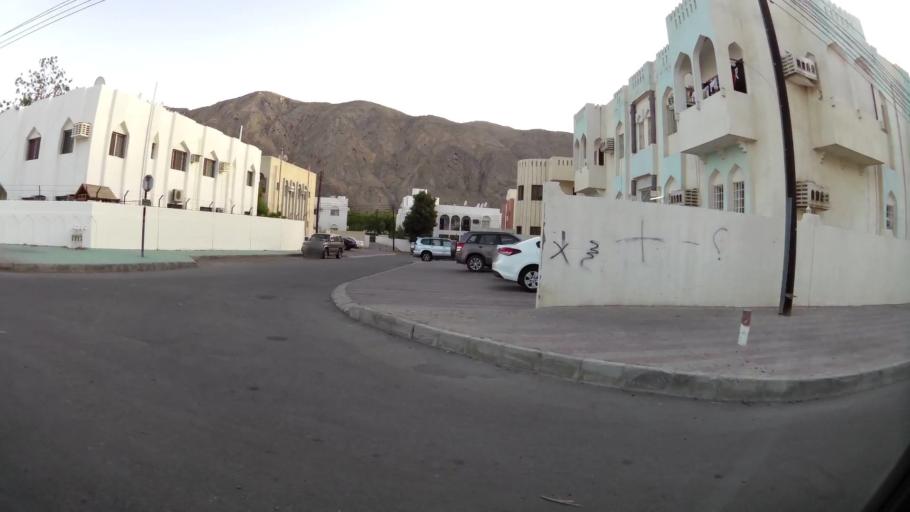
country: OM
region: Muhafazat Masqat
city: Muscat
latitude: 23.5737
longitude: 58.5692
